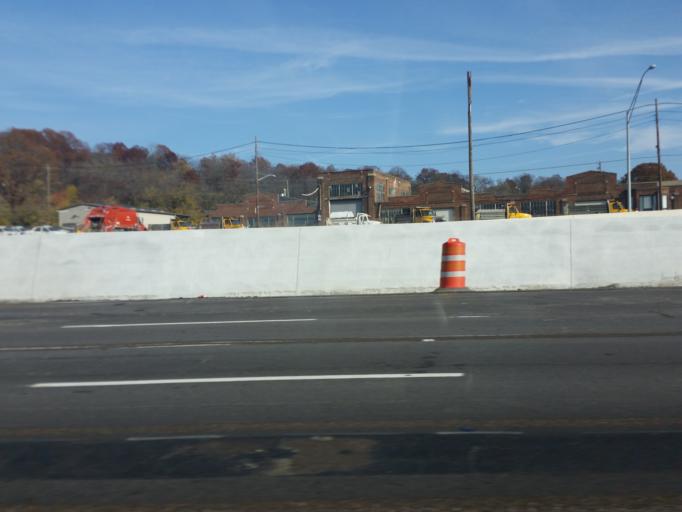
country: US
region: Ohio
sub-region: Hamilton County
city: Saint Bernard
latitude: 39.1418
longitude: -84.5353
